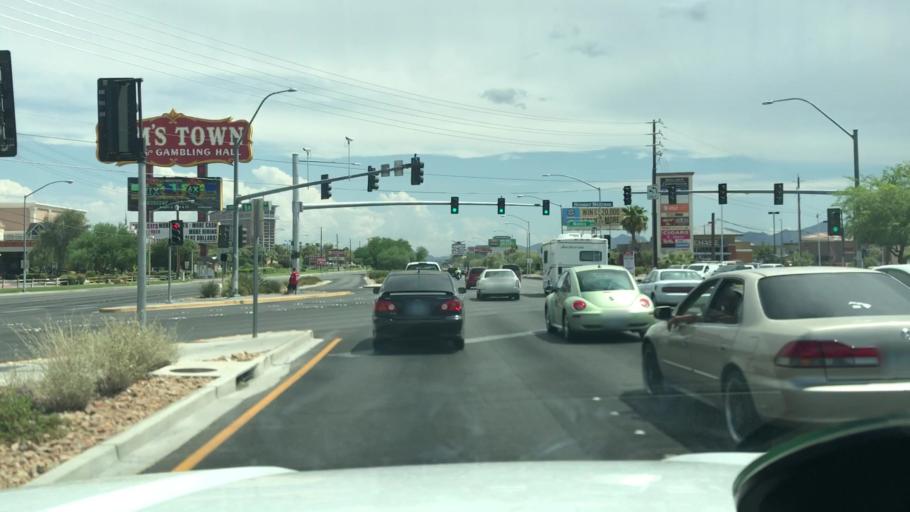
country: US
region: Nevada
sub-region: Clark County
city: Whitney
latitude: 36.1131
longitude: -115.0649
